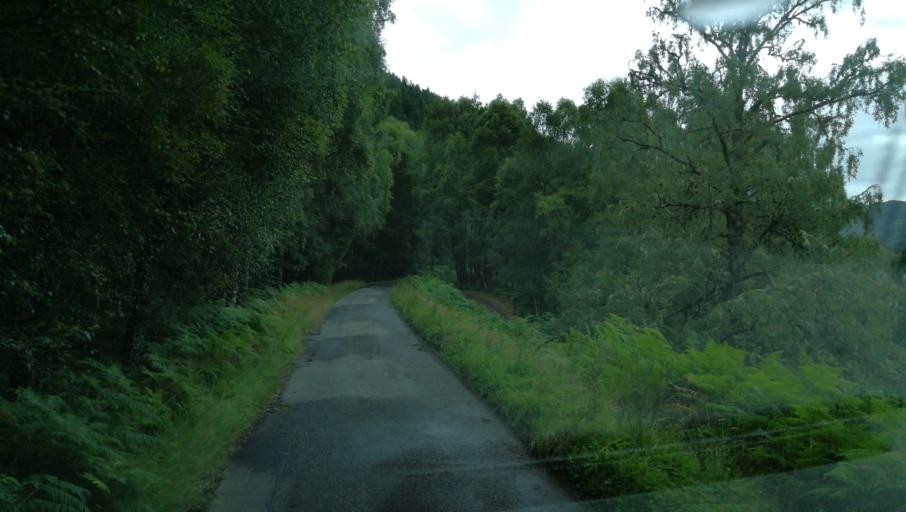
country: GB
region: Scotland
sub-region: Highland
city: Spean Bridge
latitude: 57.2943
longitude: -4.9160
